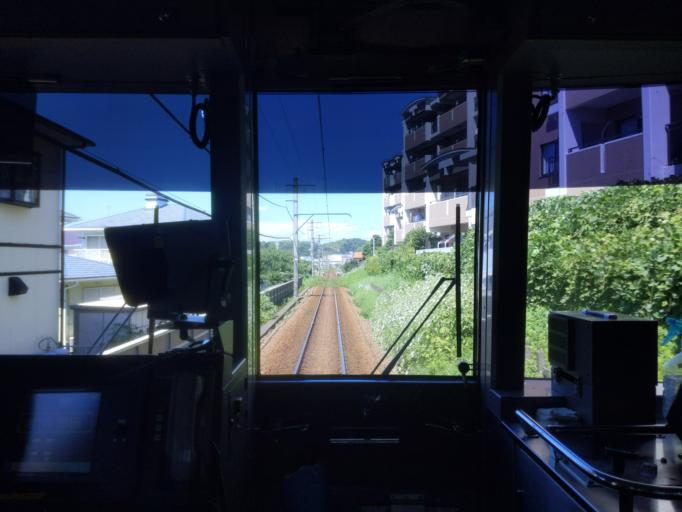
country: JP
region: Tokyo
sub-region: Machida-shi
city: Machida
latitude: 35.5358
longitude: 139.4919
